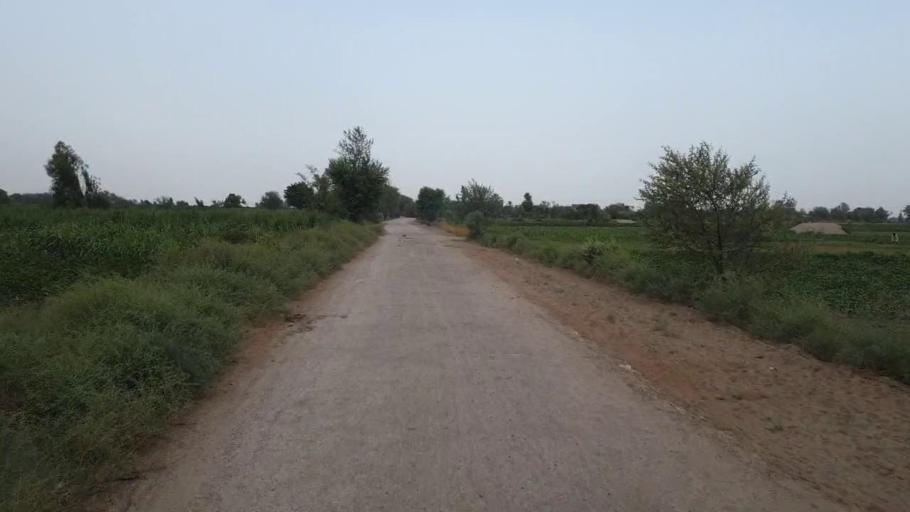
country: PK
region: Sindh
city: Bandhi
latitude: 26.5320
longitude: 68.2048
